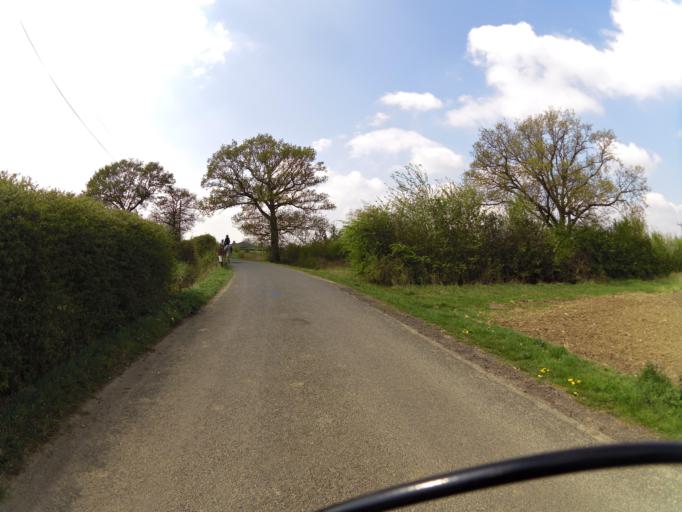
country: GB
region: England
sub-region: Suffolk
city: Hadleigh
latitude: 52.0826
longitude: 0.9742
